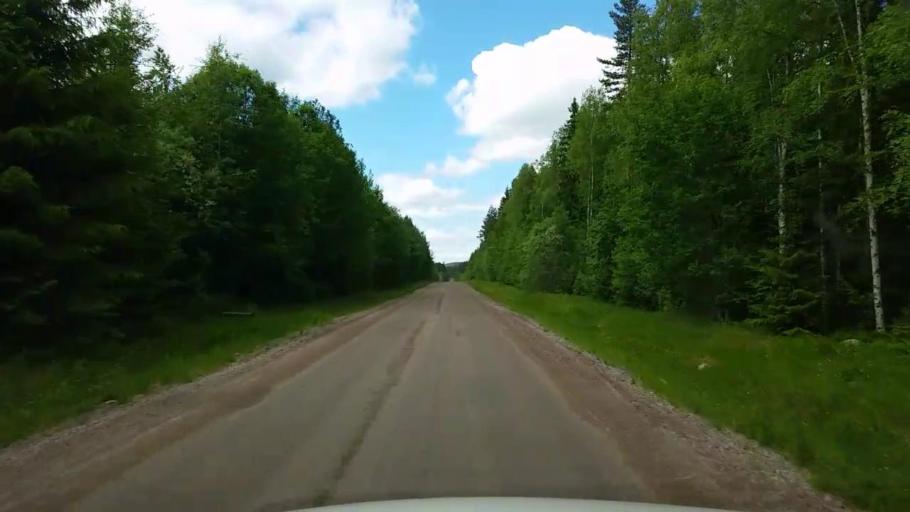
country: SE
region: Gaevleborg
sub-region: Ovanakers Kommun
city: Alfta
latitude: 61.4838
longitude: 15.9913
